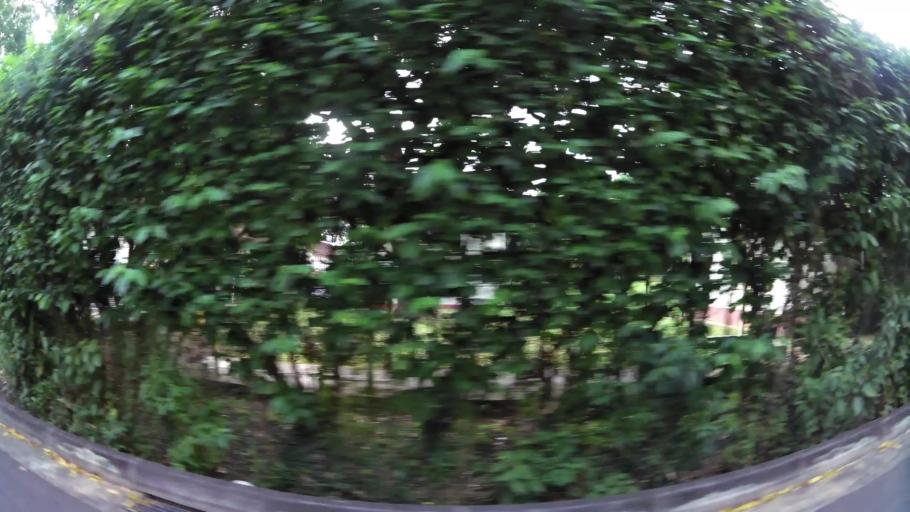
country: SG
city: Singapore
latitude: 1.3245
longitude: 103.8171
